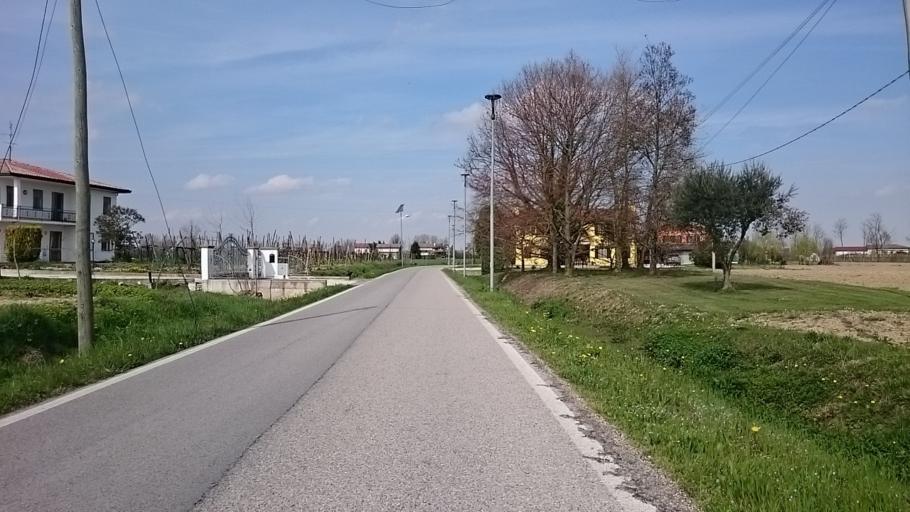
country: IT
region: Veneto
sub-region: Provincia di Padova
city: Montegrotto Terme
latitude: 45.3384
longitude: 11.8059
